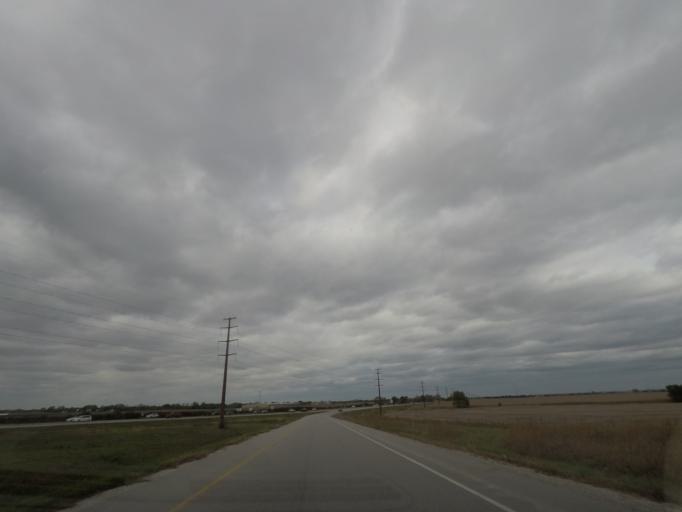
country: US
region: Iowa
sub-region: Story County
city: Huxley
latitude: 41.8793
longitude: -93.5698
